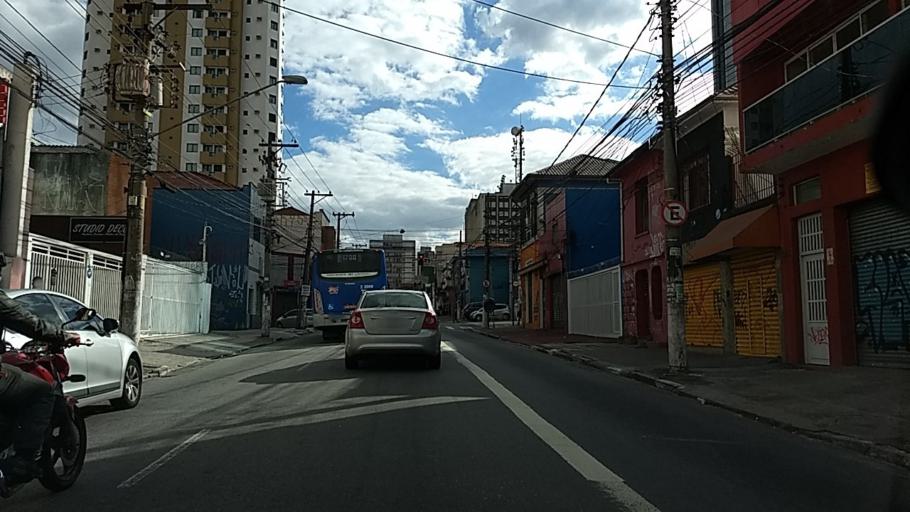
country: BR
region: Sao Paulo
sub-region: Sao Paulo
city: Sao Paulo
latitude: -23.5000
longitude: -46.6230
